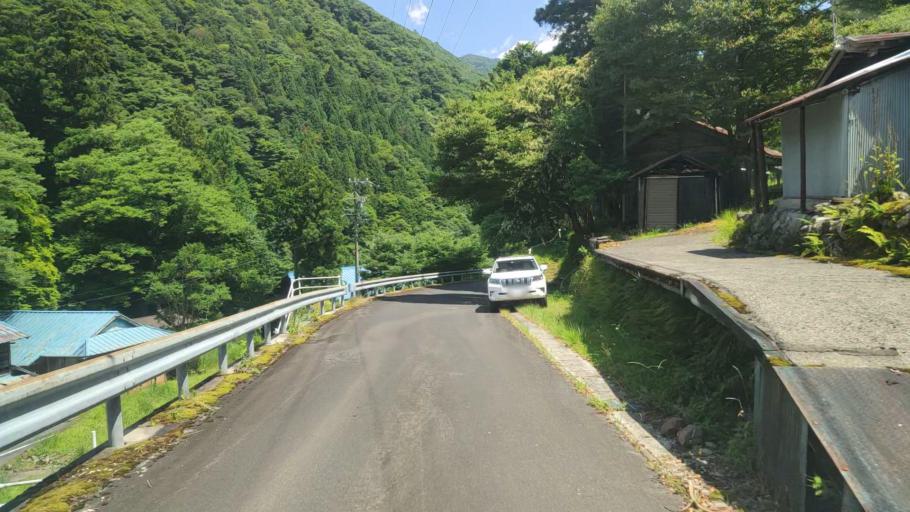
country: JP
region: Gifu
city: Godo
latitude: 35.7068
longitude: 136.5869
